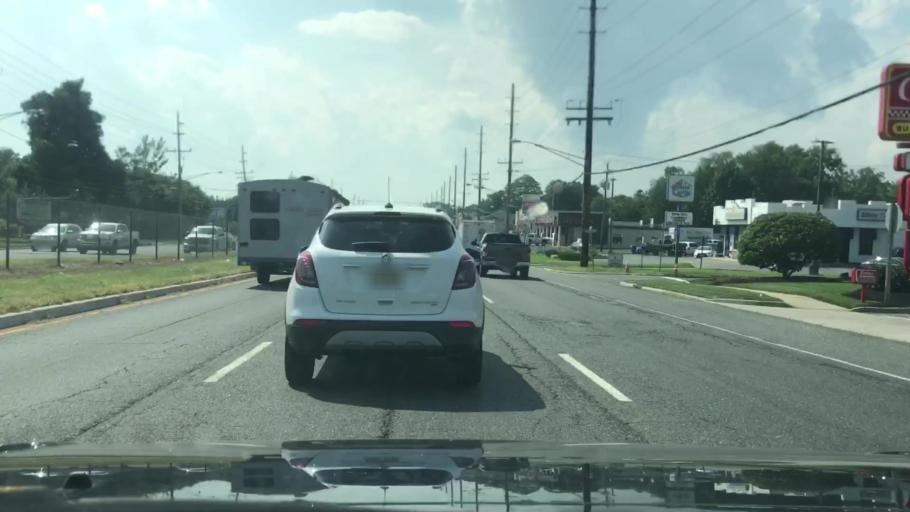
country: US
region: New Jersey
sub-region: Ocean County
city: Toms River
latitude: 39.9637
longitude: -74.1889
